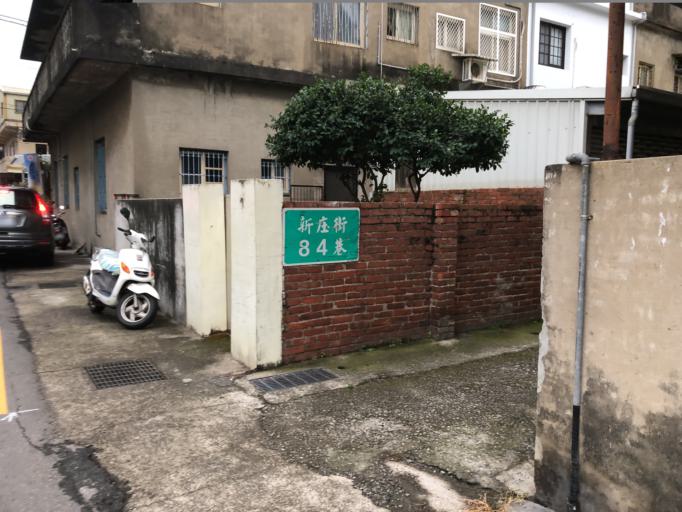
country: TW
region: Taiwan
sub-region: Miaoli
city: Miaoli
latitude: 24.5547
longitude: 120.8227
